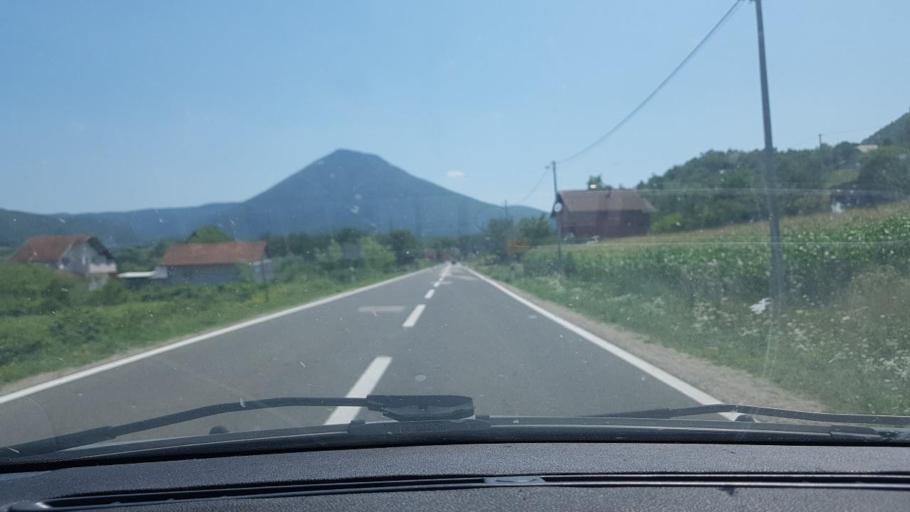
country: BA
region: Federation of Bosnia and Herzegovina
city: Bihac
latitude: 44.7675
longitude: 15.9444
